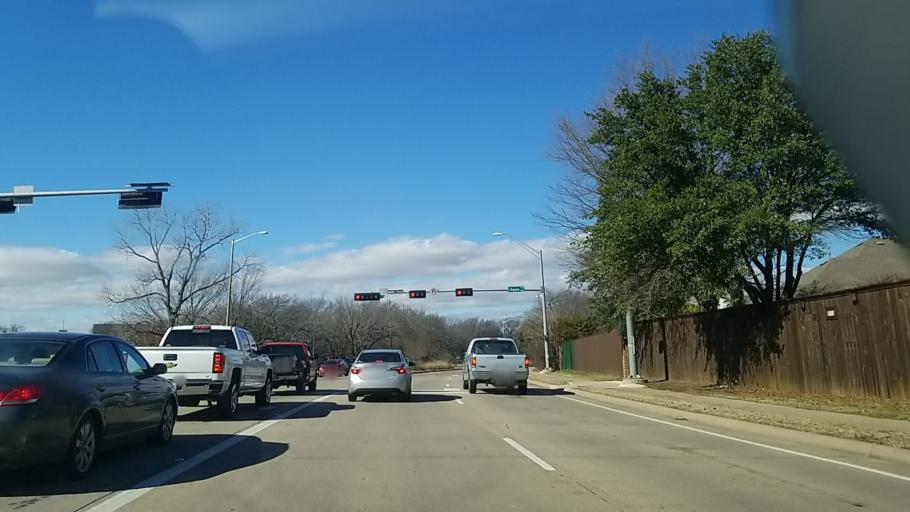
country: US
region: Texas
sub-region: Denton County
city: Denton
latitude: 33.1762
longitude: -97.1221
